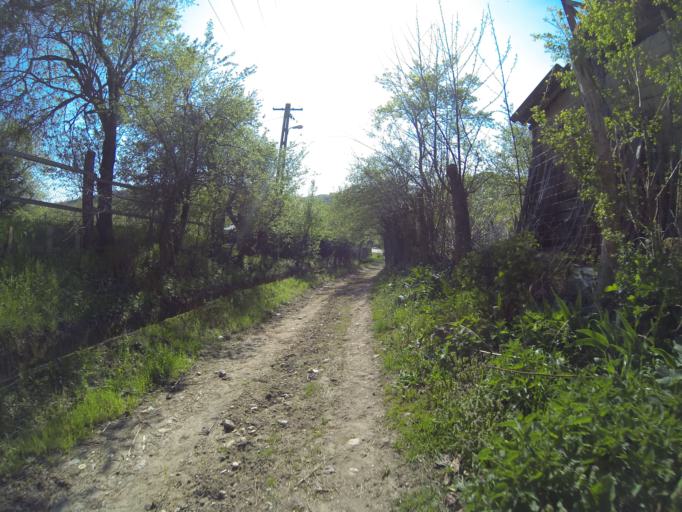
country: RO
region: Gorj
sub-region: Comuna Crusetu
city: Crusetu
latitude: 44.6118
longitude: 23.6215
